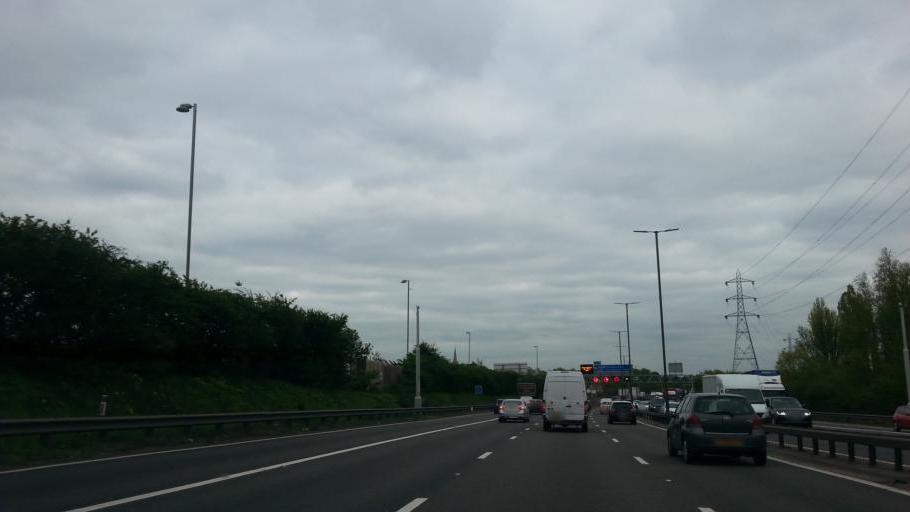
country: GB
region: England
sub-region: City and Borough of Birmingham
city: Hockley
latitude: 52.5267
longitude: -1.8905
